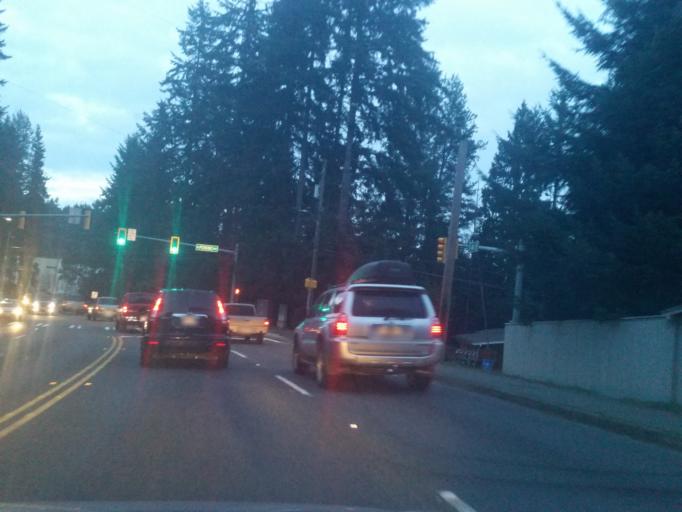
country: US
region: Washington
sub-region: Snohomish County
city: Mountlake Terrace
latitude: 47.7655
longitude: -122.3139
